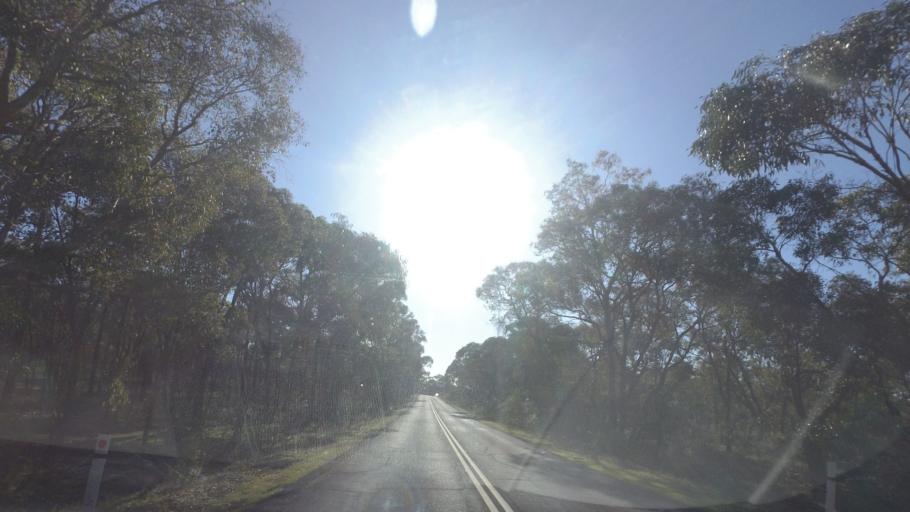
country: AU
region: Victoria
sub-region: Greater Bendigo
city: Kangaroo Flat
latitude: -36.8359
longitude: 144.2791
